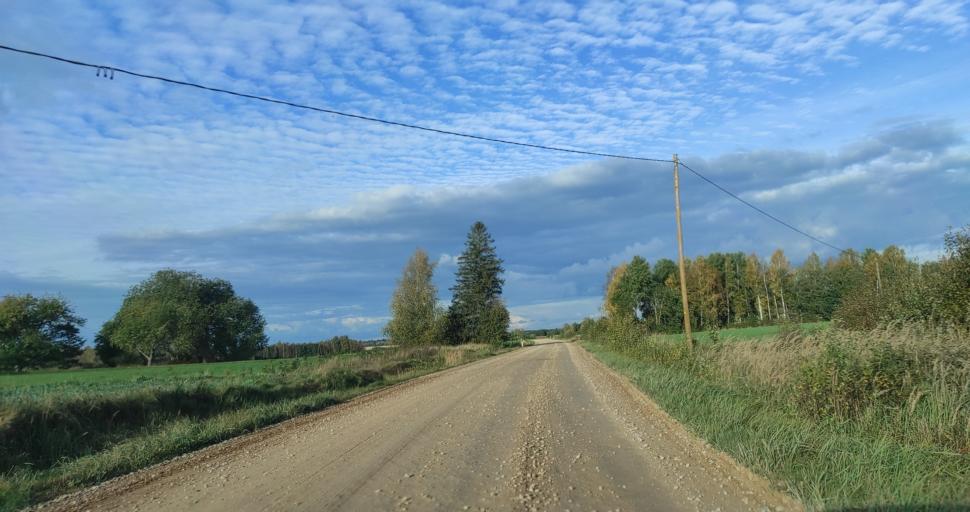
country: LV
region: Aizpute
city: Aizpute
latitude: 56.7469
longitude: 21.8108
